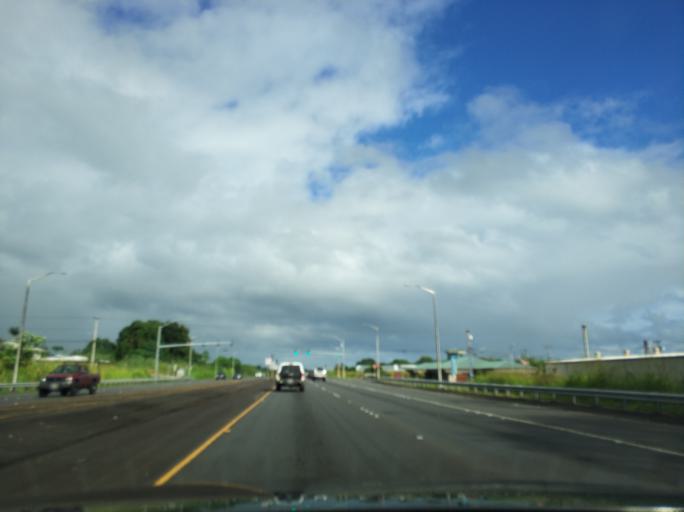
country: US
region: Hawaii
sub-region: Hawaii County
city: Kea'au
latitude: 19.6252
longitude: -155.0324
